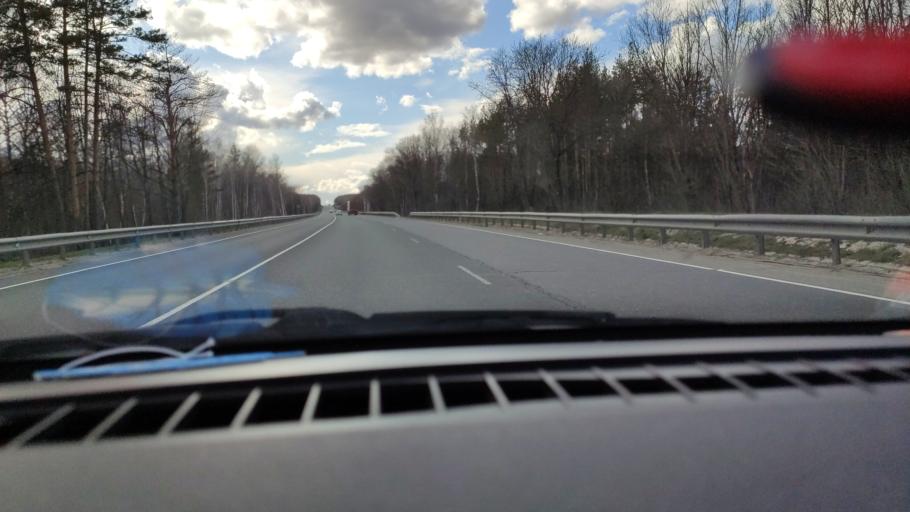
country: RU
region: Saratov
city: Vol'sk
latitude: 52.1067
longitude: 47.4223
